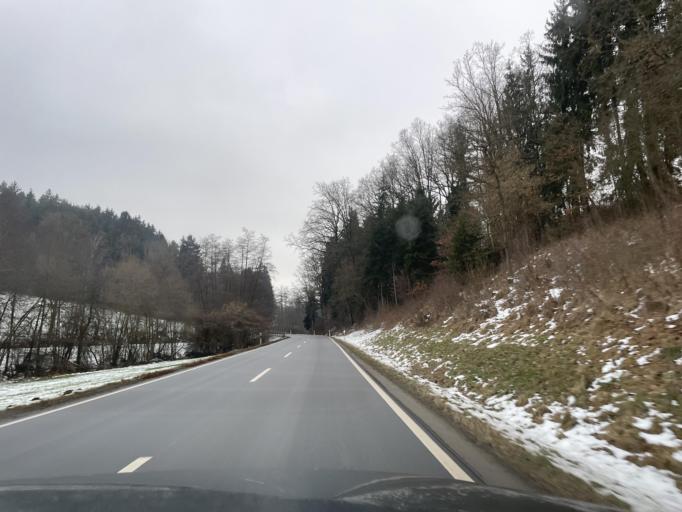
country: DE
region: Bavaria
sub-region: Lower Bavaria
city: Viechtach
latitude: 49.0568
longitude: 12.8902
